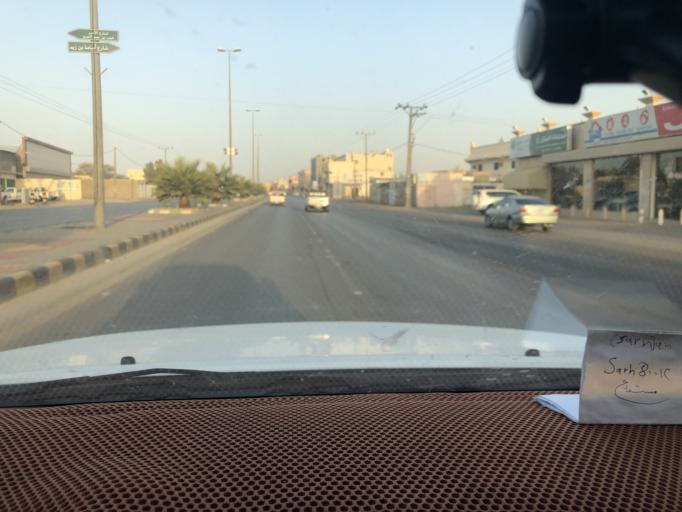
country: SA
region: Ar Riyad
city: As Sulayyil
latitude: 20.4495
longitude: 44.8500
